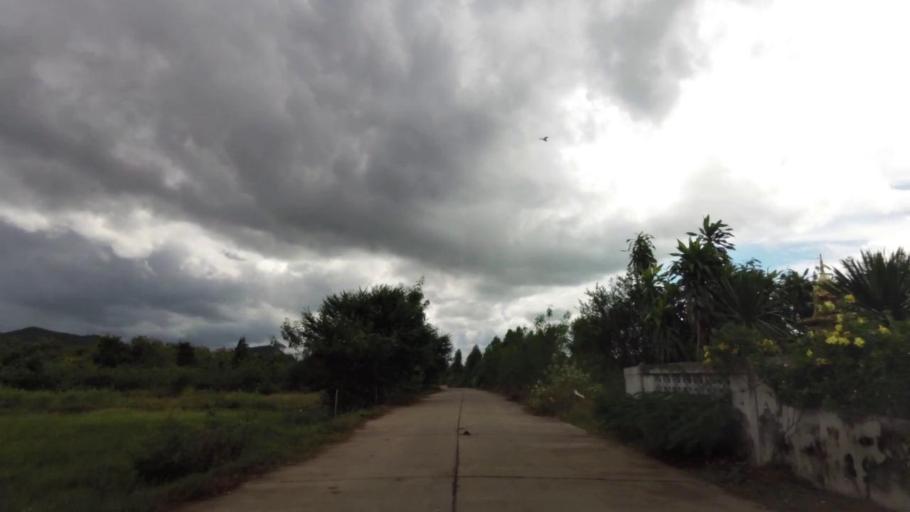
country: TH
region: Nakhon Sawan
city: Phai Sali
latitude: 15.6026
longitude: 100.6775
